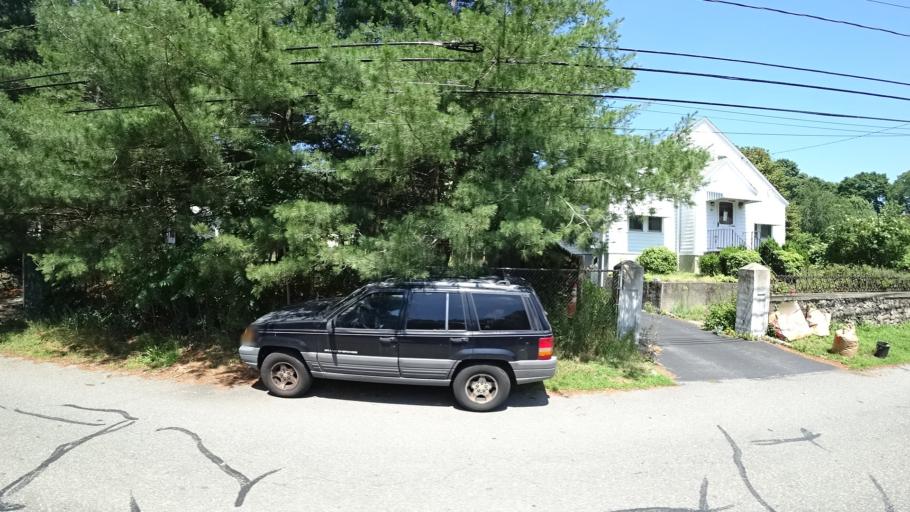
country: US
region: Massachusetts
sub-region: Norfolk County
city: Dedham
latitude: 42.2514
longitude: -71.1529
